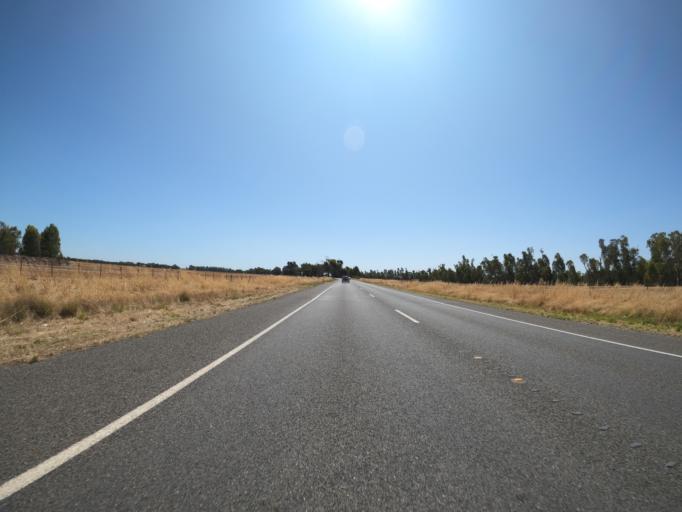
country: AU
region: Victoria
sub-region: Moira
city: Yarrawonga
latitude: -36.0231
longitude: 146.1414
